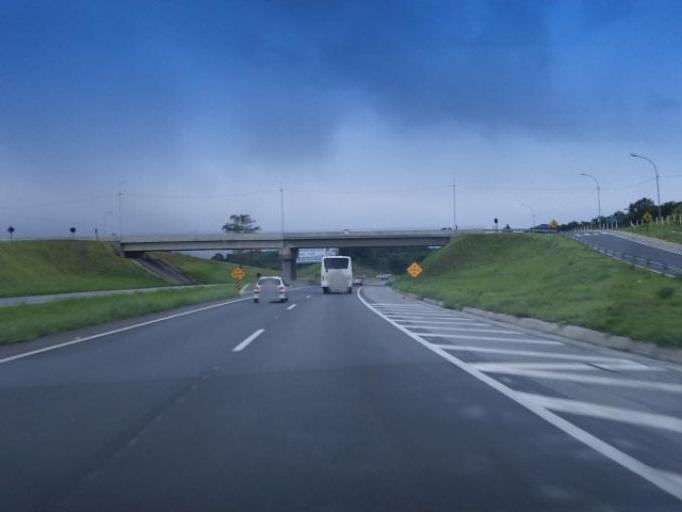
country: BR
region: Sao Paulo
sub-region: Miracatu
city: Miracatu
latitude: -24.2958
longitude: -47.4805
